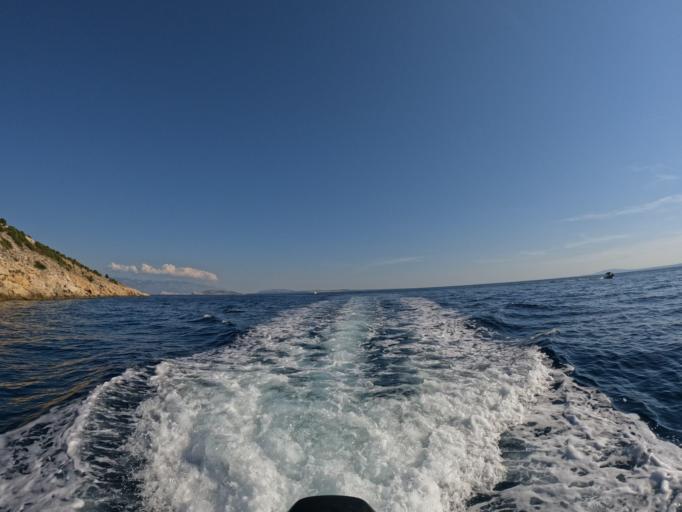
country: HR
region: Primorsko-Goranska
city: Punat
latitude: 44.9658
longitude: 14.6479
